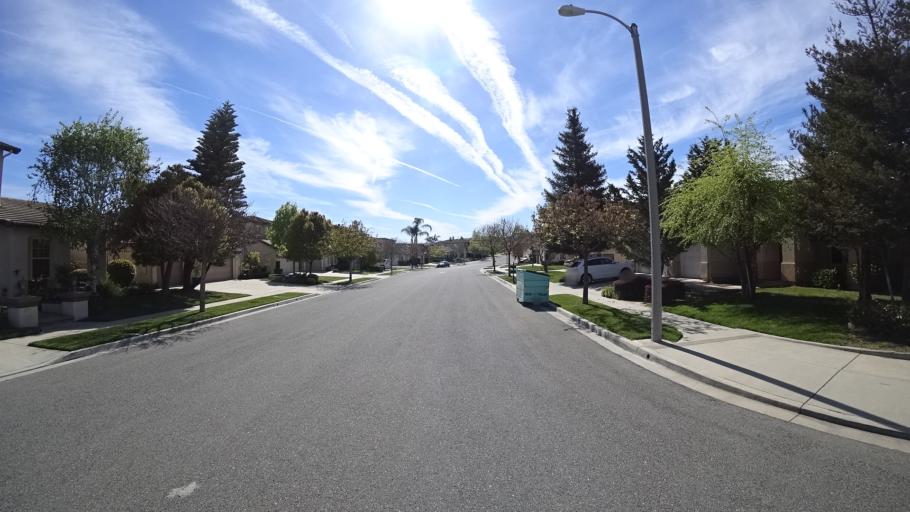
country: US
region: California
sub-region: Ventura County
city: Casa Conejo
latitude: 34.1726
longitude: -118.9805
